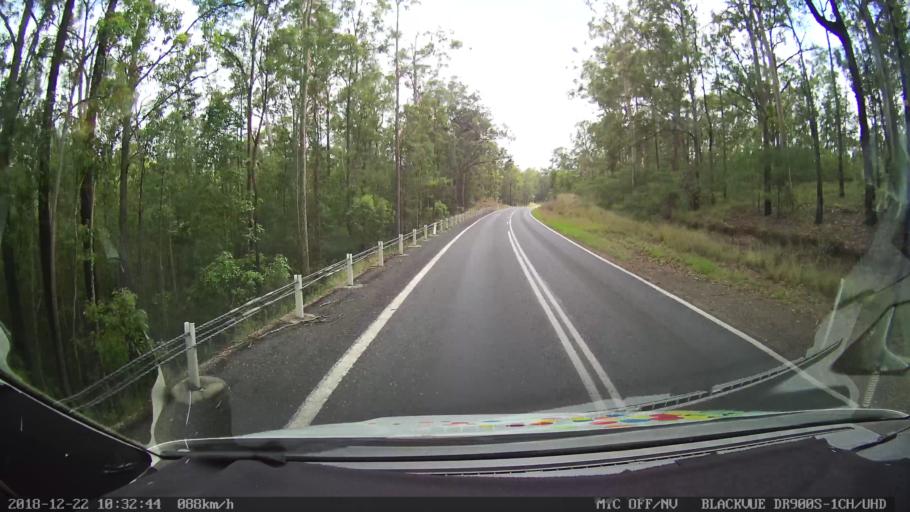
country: AU
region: New South Wales
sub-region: Clarence Valley
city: South Grafton
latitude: -29.6191
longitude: 152.6445
